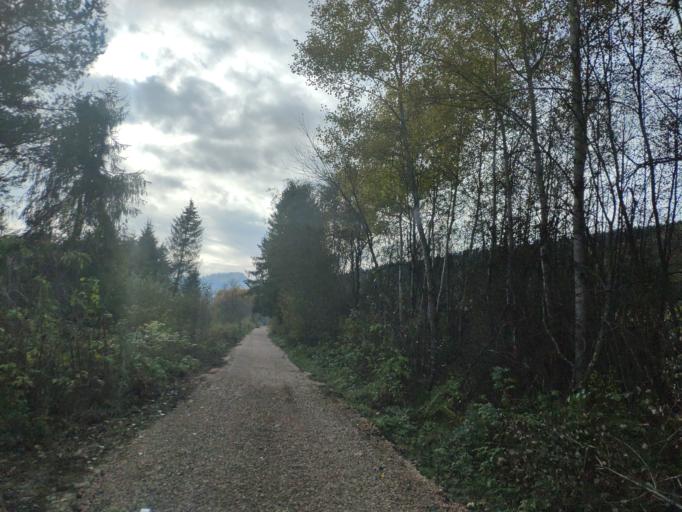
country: SK
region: Kosicky
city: Spisska Nova Ves
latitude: 48.8274
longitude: 20.6247
